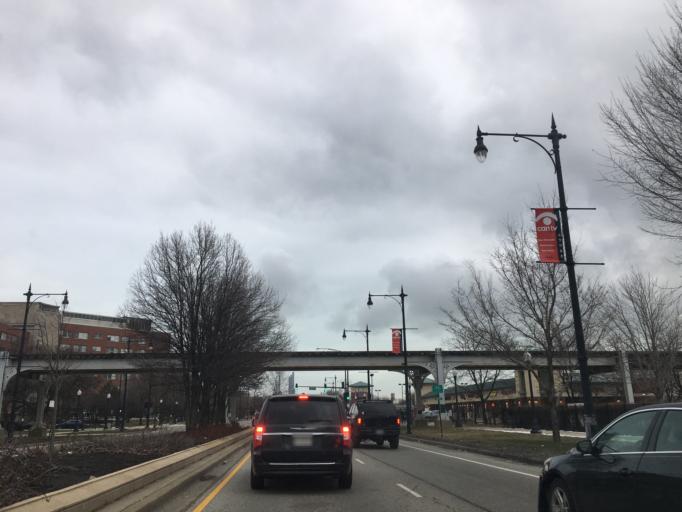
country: US
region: Illinois
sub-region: Cook County
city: Chicago
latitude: 41.8667
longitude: -87.6700
